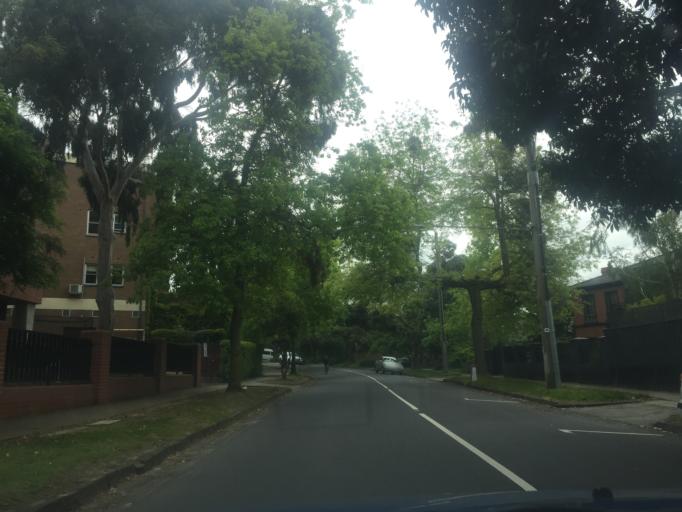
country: AU
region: Victoria
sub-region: Boroondara
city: Kew
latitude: -37.8124
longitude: 145.0344
